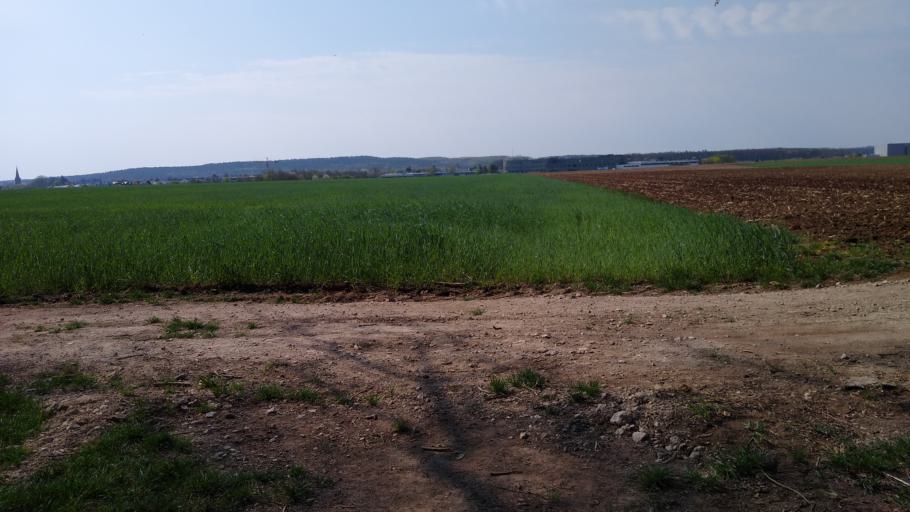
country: DE
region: Bavaria
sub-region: Regierungsbezirk Mittelfranken
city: Obermichelbach
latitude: 49.5023
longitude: 10.9170
